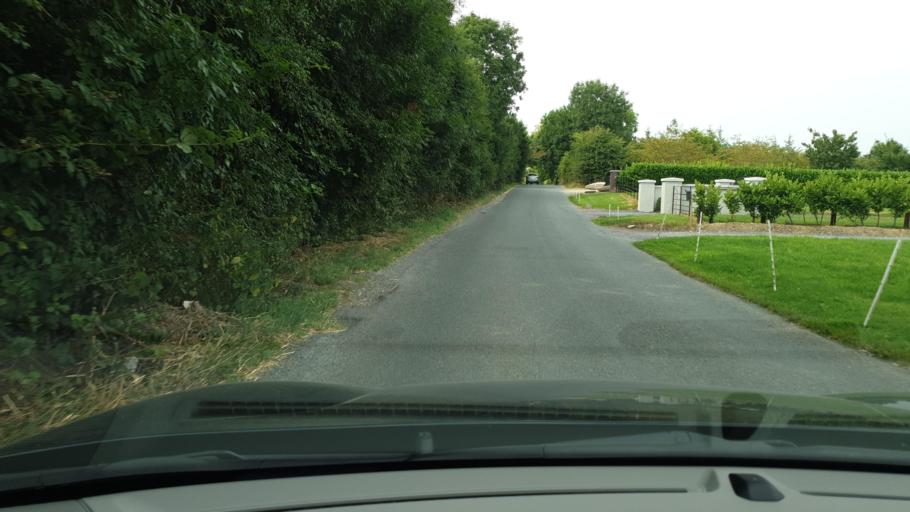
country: IE
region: Leinster
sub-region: An Mhi
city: Athboy
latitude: 53.6677
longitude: -6.9125
